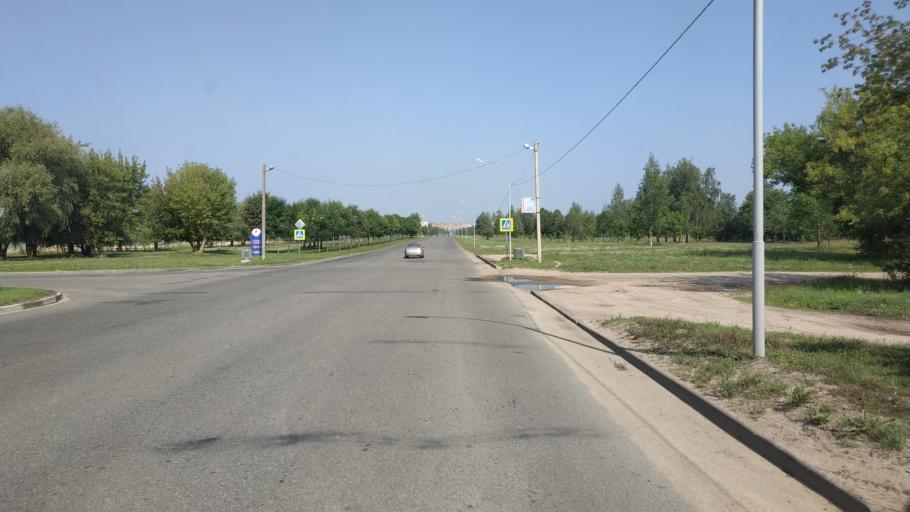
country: BY
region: Mogilev
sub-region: Mahilyowski Rayon
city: Veyno
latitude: 53.8576
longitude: 30.3288
